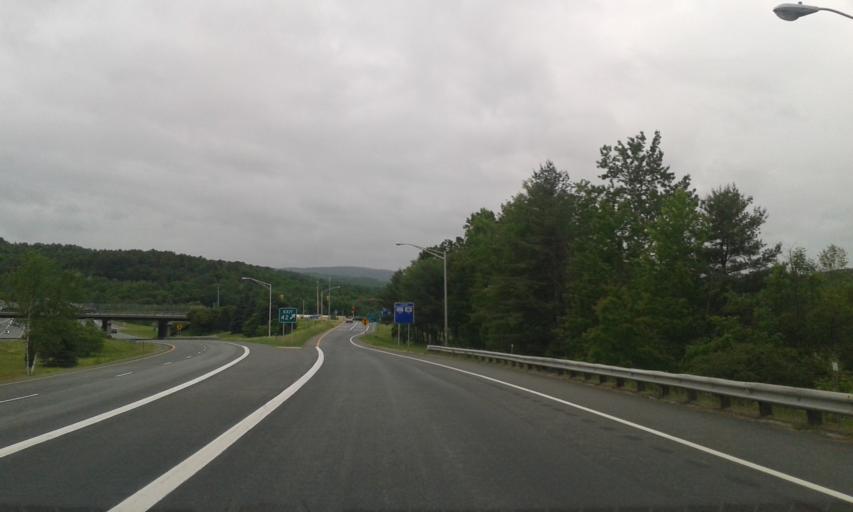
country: US
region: New Hampshire
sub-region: Grafton County
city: Littleton
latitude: 44.3107
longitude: -71.8001
